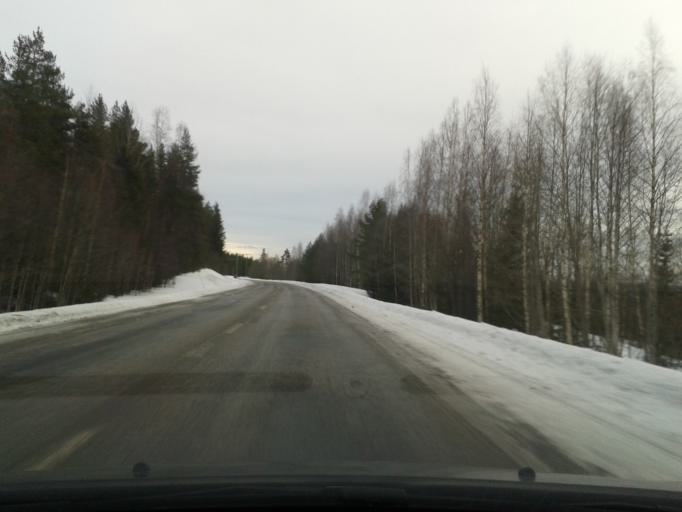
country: SE
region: Vaesternorrland
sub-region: Solleftea Kommun
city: As
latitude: 63.5207
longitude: 16.8341
